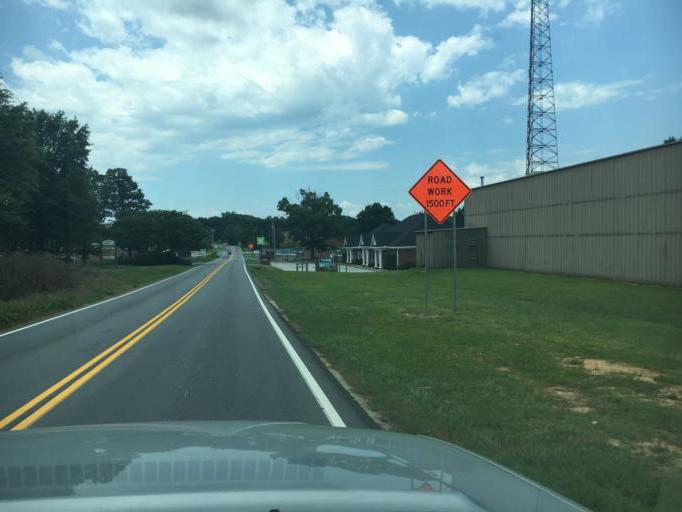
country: US
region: South Carolina
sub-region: Greenville County
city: Five Forks
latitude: 34.8687
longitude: -82.2472
